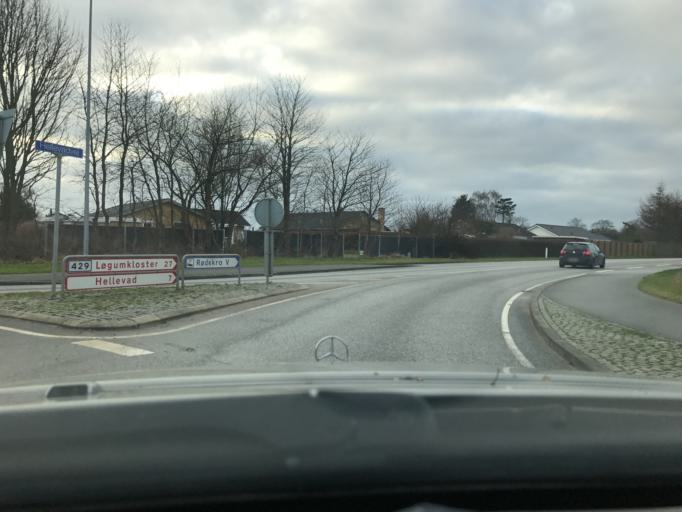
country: DK
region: South Denmark
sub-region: Aabenraa Kommune
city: Rodekro
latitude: 55.0747
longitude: 9.3400
